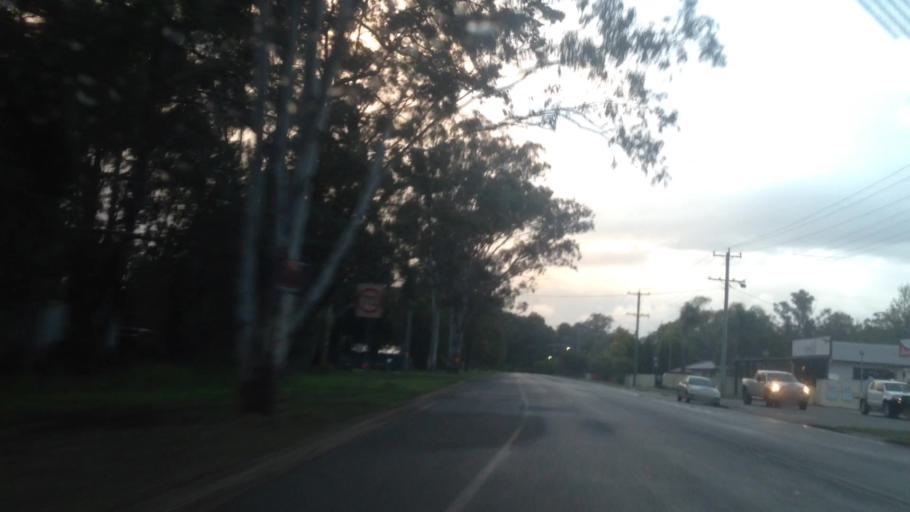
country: AU
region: New South Wales
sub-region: Lake Macquarie Shire
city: Cooranbong
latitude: -33.0877
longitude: 151.4501
